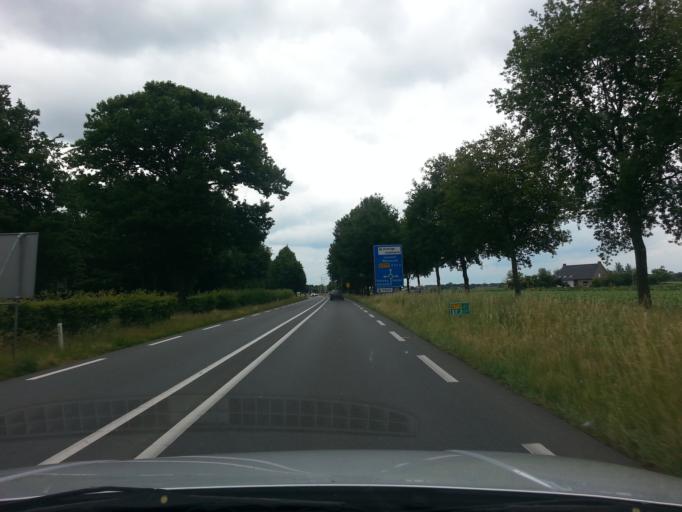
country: NL
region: Limburg
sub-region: Gemeente Venray
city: Venray
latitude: 51.5130
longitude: 5.9583
